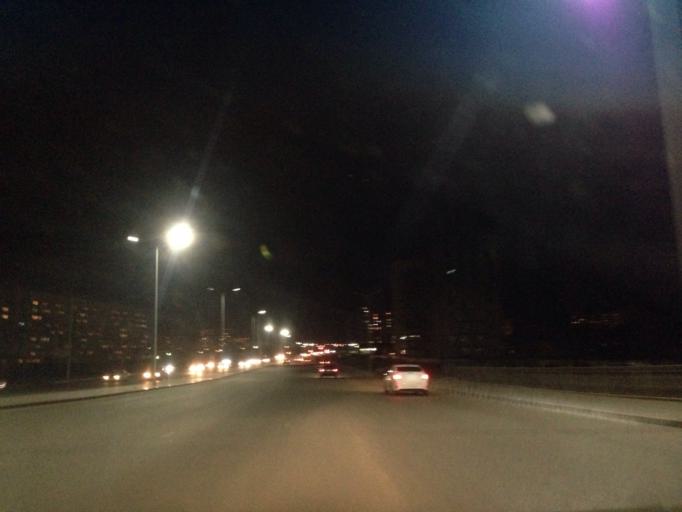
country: KZ
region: Astana Qalasy
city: Astana
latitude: 51.1662
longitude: 71.3753
